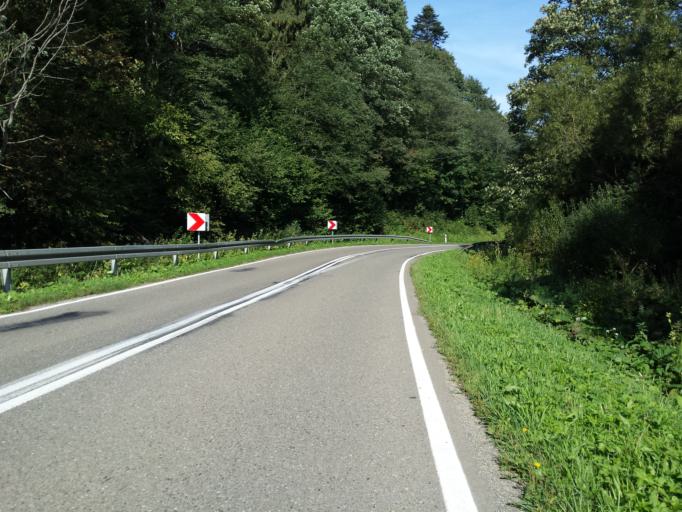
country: PL
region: Subcarpathian Voivodeship
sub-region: Powiat leski
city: Baligrod
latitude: 49.2843
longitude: 22.2765
